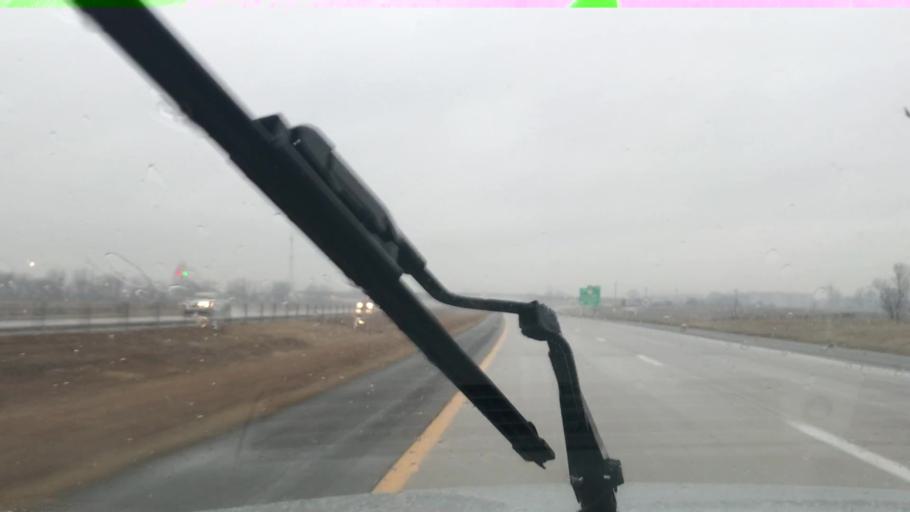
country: US
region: Kentucky
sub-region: Christian County
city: Oak Grove
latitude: 36.6786
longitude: -87.3973
